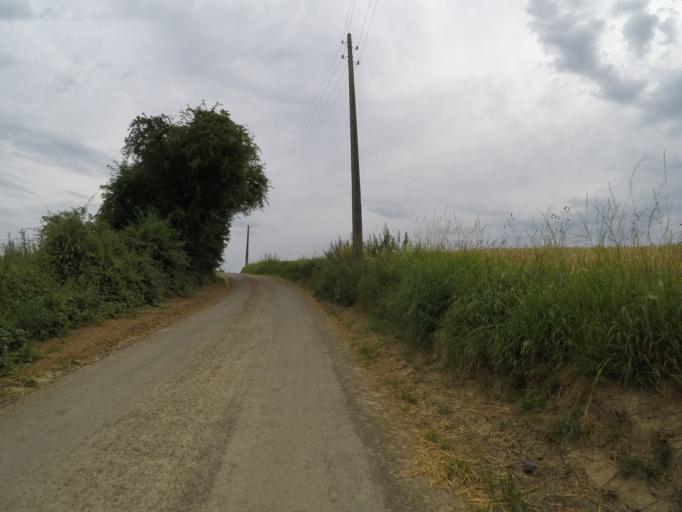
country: BE
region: Wallonia
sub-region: Province de Namur
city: Assesse
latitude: 50.3048
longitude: 5.0004
